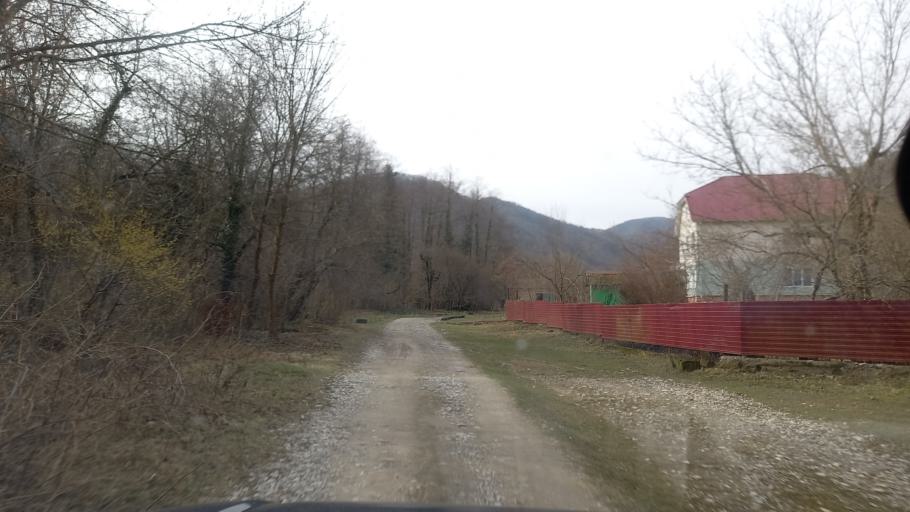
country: RU
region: Krasnodarskiy
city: Dzhubga
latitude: 44.4156
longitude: 38.7212
